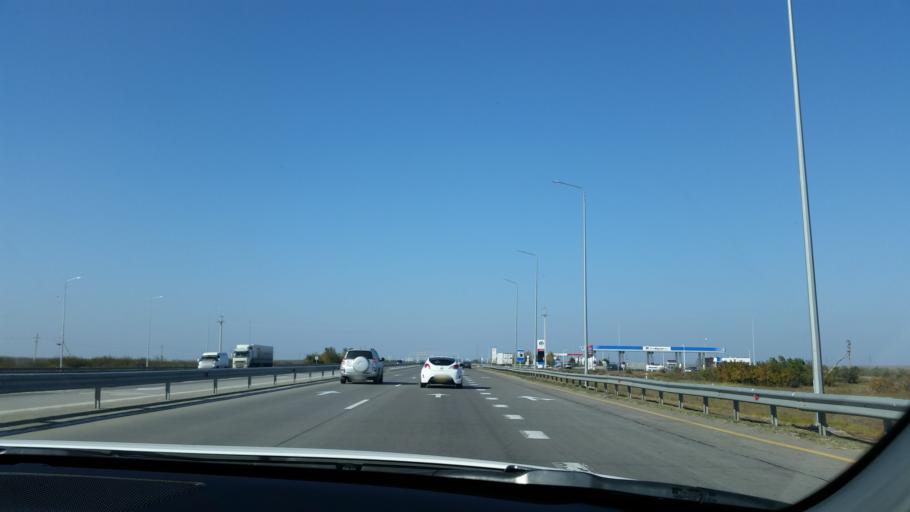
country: KZ
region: Astana Qalasy
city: Astana
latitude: 51.2662
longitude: 71.3697
